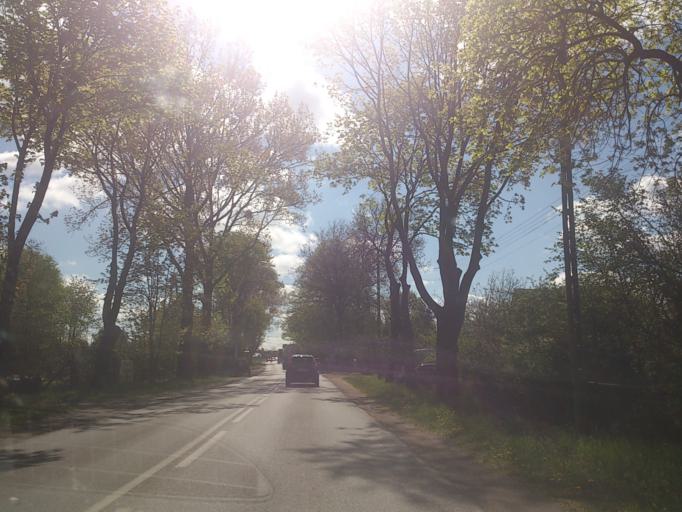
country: PL
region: Warmian-Masurian Voivodeship
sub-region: Powiat dzialdowski
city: Dzialdowo
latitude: 53.2274
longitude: 20.1960
